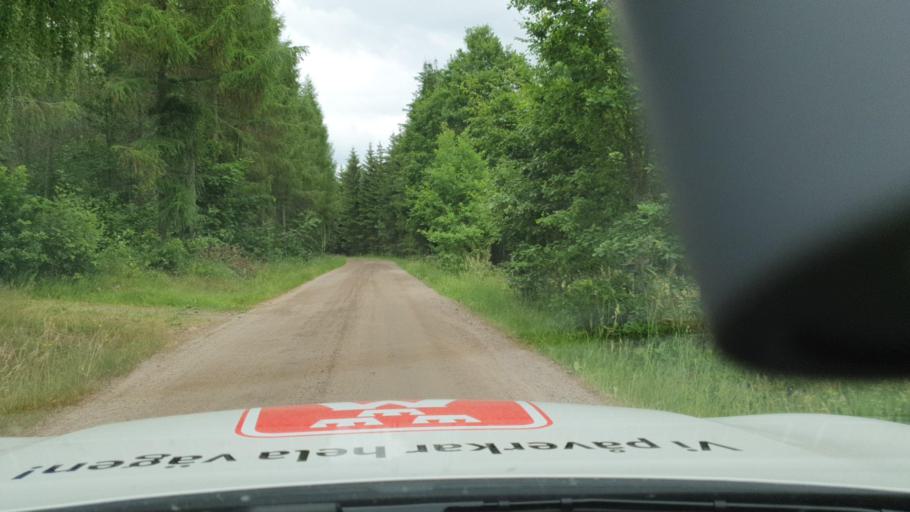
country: SE
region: Vaestra Goetaland
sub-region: Hjo Kommun
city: Hjo
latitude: 58.2002
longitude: 14.1766
